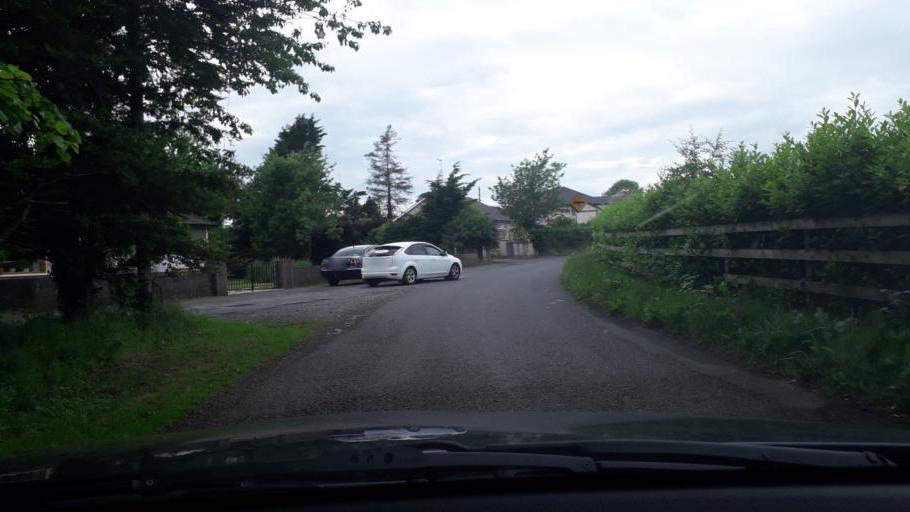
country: IE
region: Leinster
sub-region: Kildare
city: Castledermot
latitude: 52.9128
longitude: -6.8356
